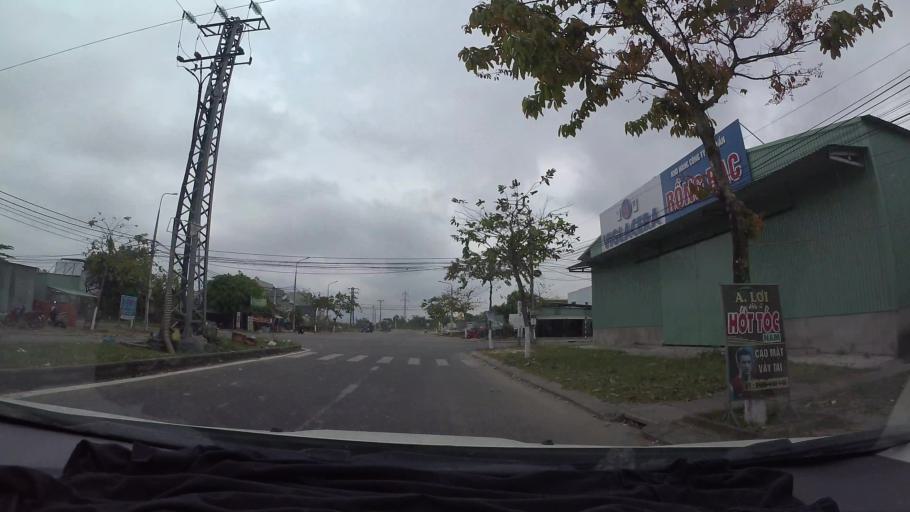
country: VN
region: Da Nang
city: Thanh Khe
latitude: 16.0439
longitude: 108.1764
